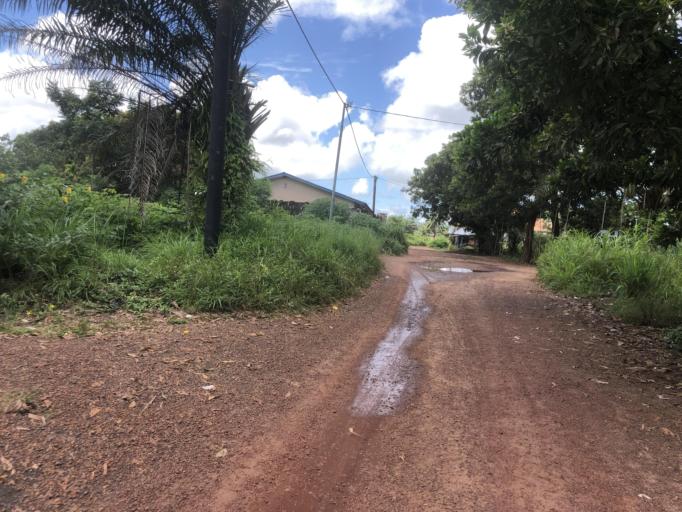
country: SL
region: Northern Province
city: Makeni
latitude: 8.8614
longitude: -12.0461
